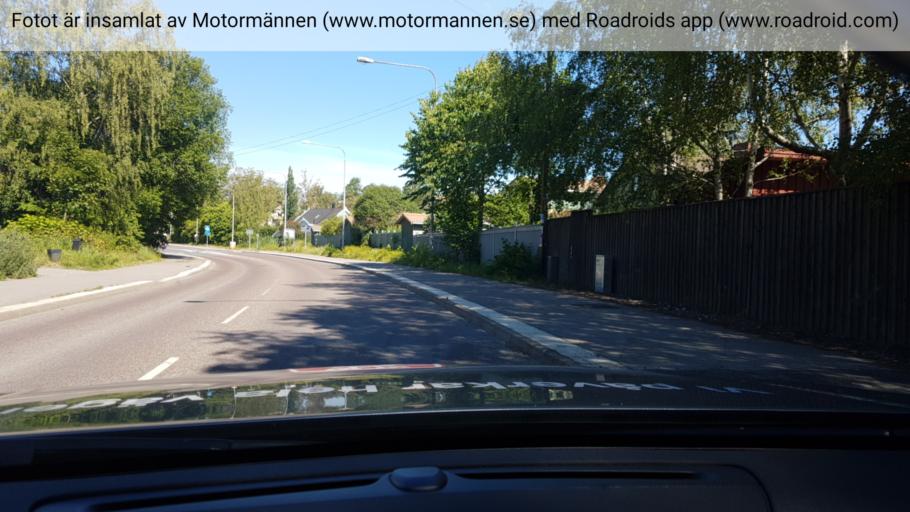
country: SE
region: Stockholm
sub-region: Huddinge Kommun
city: Huddinge
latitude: 59.2583
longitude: 17.9787
